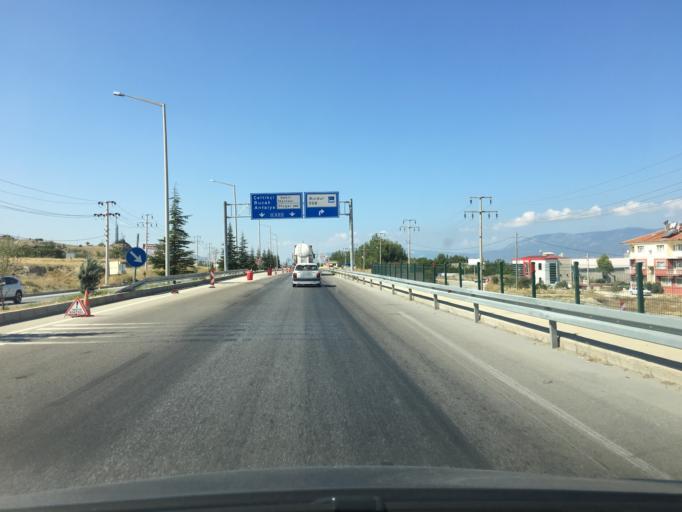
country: TR
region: Burdur
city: Burdur
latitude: 37.7492
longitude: 30.3252
